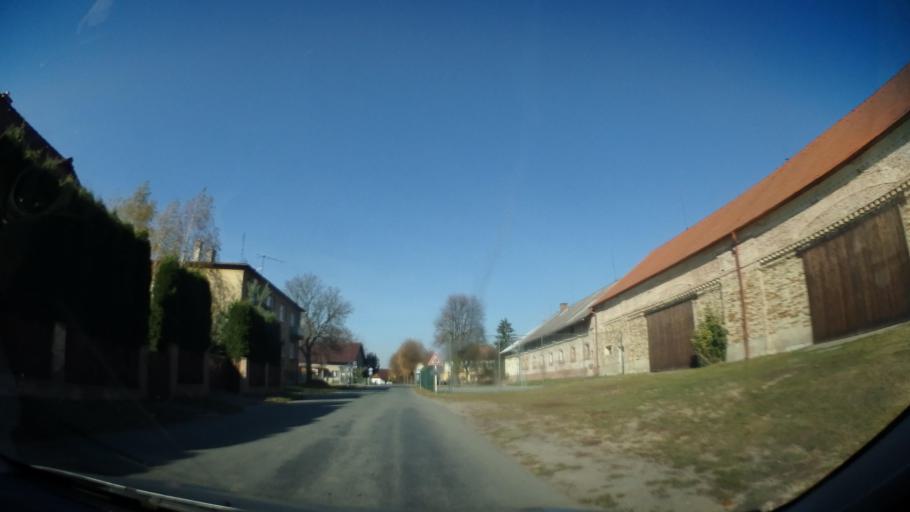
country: CZ
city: Ceske Mezirici
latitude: 50.2346
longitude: 16.0383
